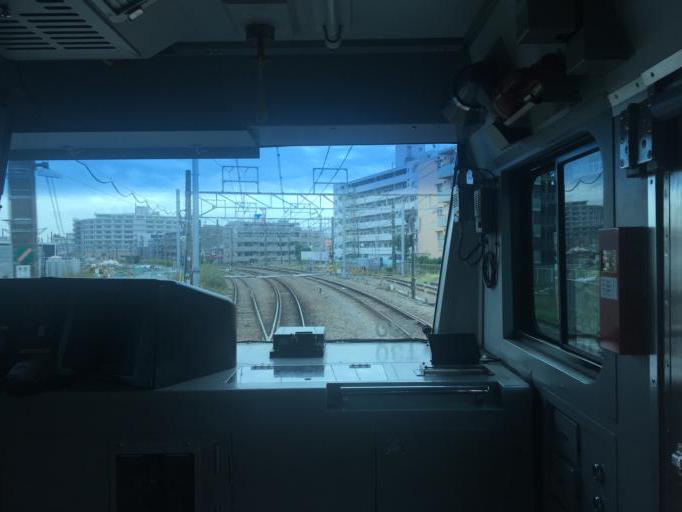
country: JP
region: Tokyo
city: Fussa
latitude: 35.7192
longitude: 139.3450
